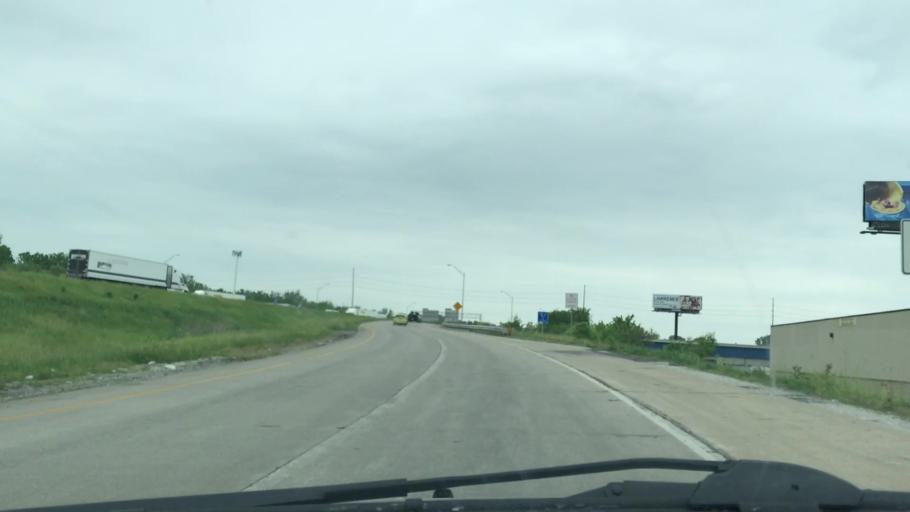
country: US
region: Indiana
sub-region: Marion County
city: Lawrence
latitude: 39.8331
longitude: -86.0353
